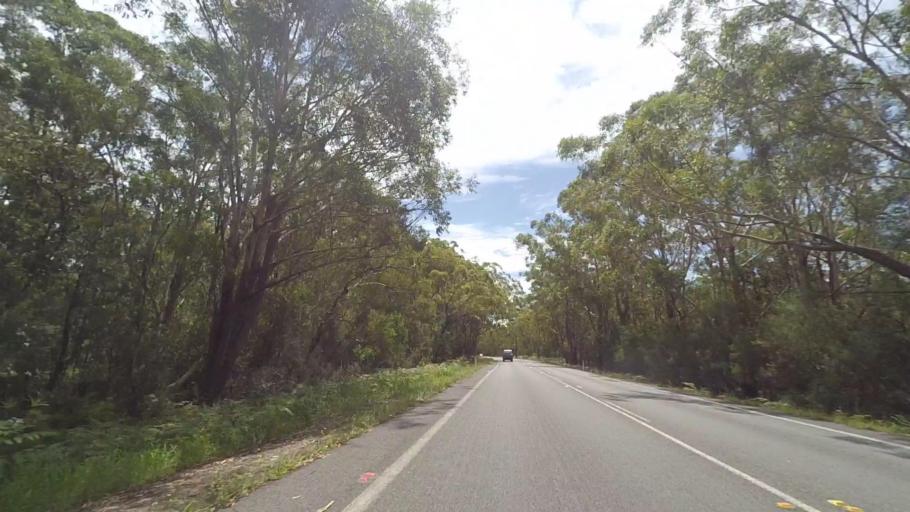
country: AU
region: New South Wales
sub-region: Port Stephens Shire
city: Medowie
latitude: -32.7733
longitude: 151.8679
